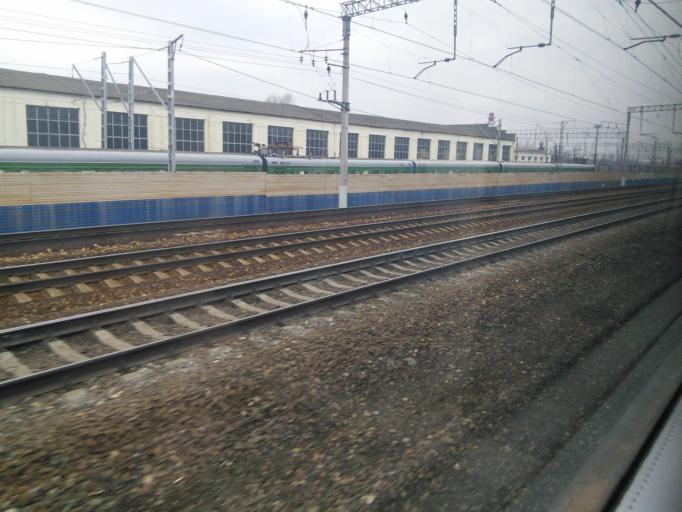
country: RU
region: Moskovskaya
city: Domodedovo
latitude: 55.4267
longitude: 37.7827
